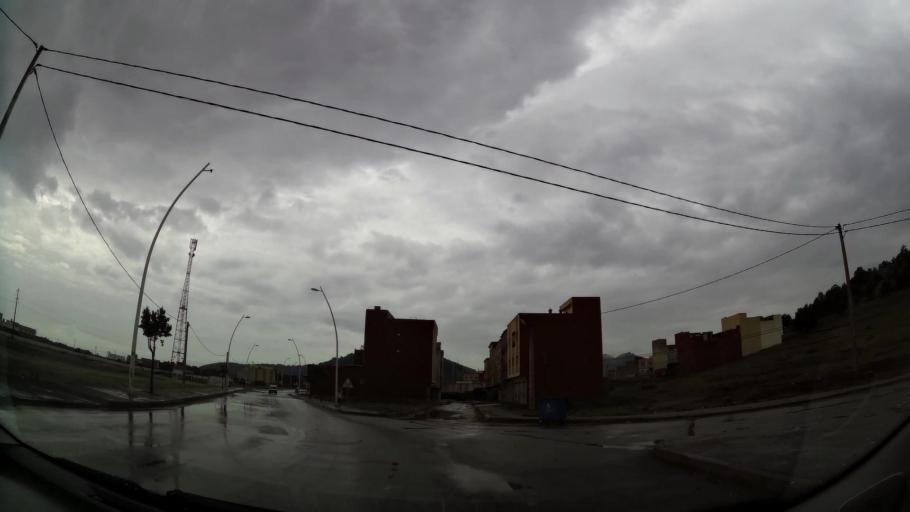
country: MA
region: Oriental
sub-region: Nador
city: Nador
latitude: 35.1468
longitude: -2.9781
